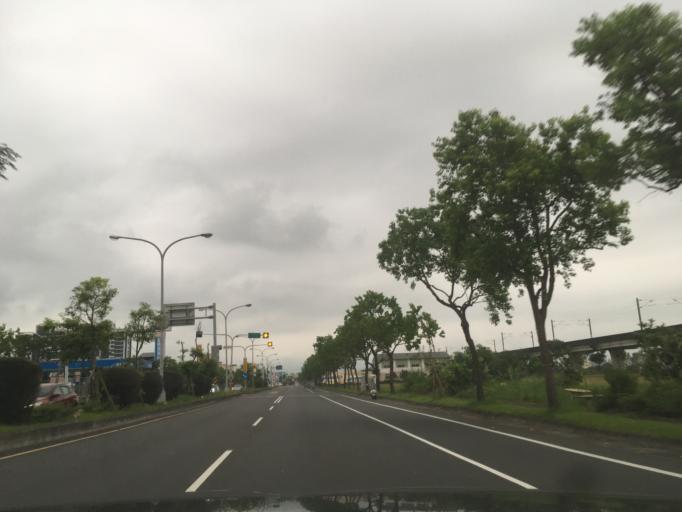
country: TW
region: Taiwan
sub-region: Yilan
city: Yilan
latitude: 24.7346
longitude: 121.7630
